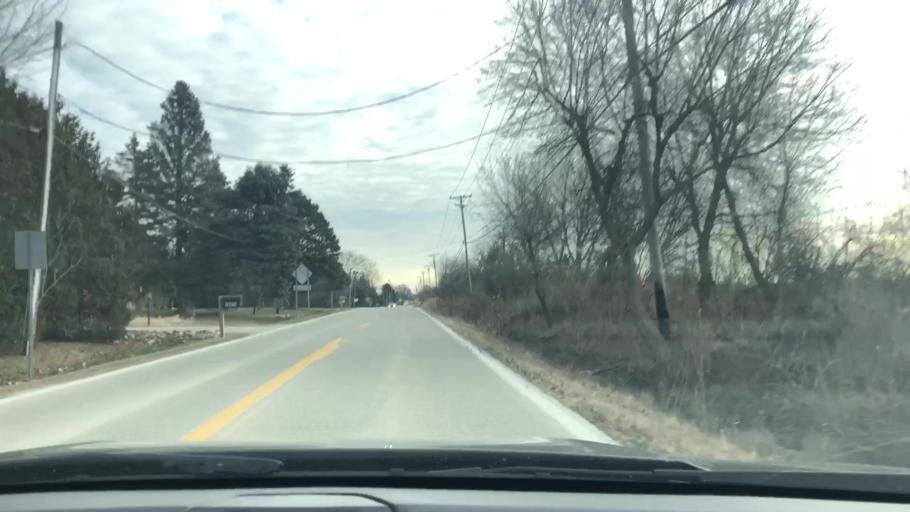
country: US
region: Michigan
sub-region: Macomb County
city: Shelby
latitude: 42.7291
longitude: -83.0031
